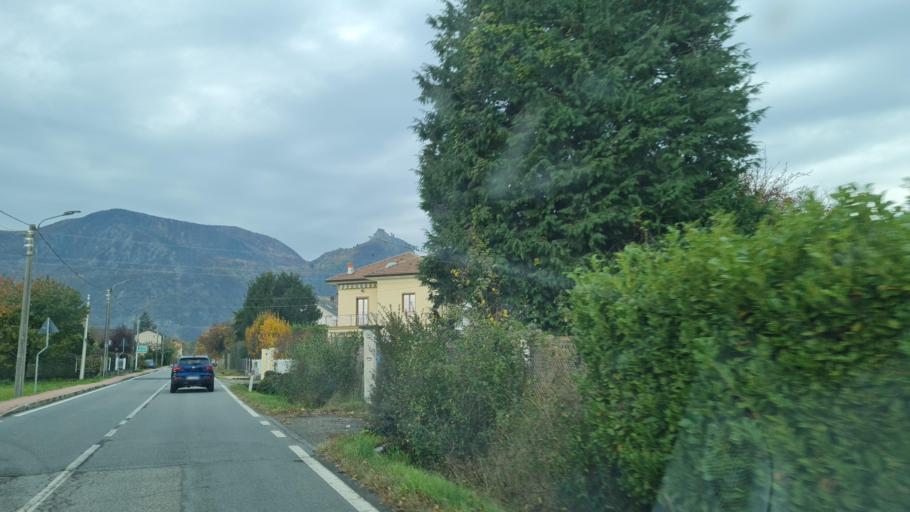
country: IT
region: Piedmont
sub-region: Provincia di Torino
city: Villar Dora
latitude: 45.1087
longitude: 7.3822
